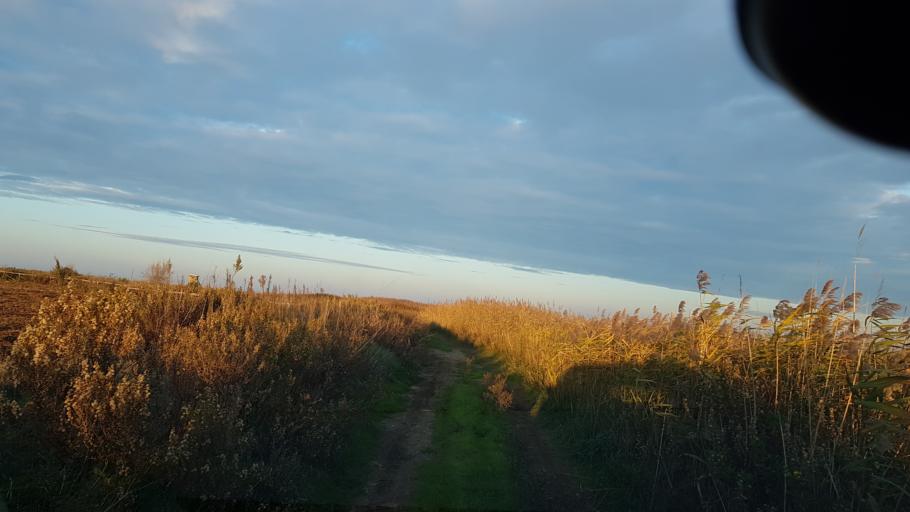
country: IT
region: Apulia
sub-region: Provincia di Brindisi
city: La Rosa
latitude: 40.6126
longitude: 18.0188
